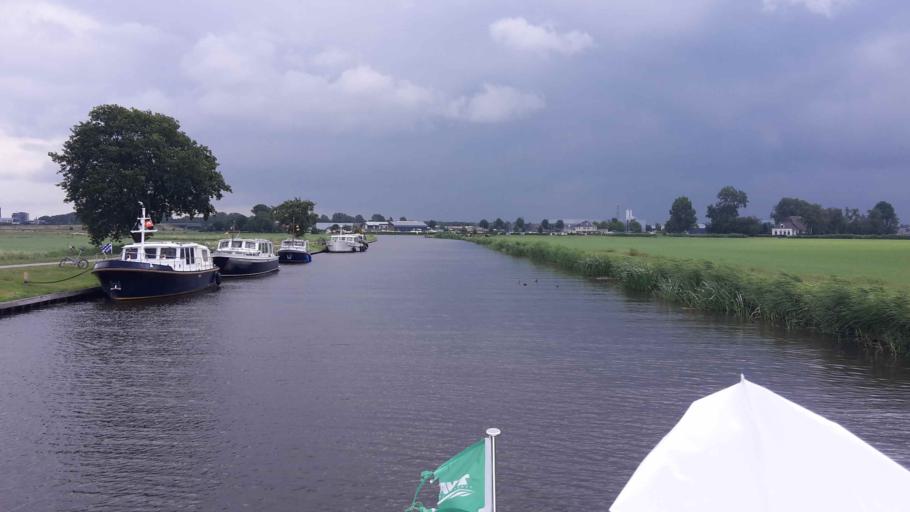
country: NL
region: Overijssel
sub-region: Gemeente Steenwijkerland
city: Tuk
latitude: 52.7865
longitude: 6.0793
